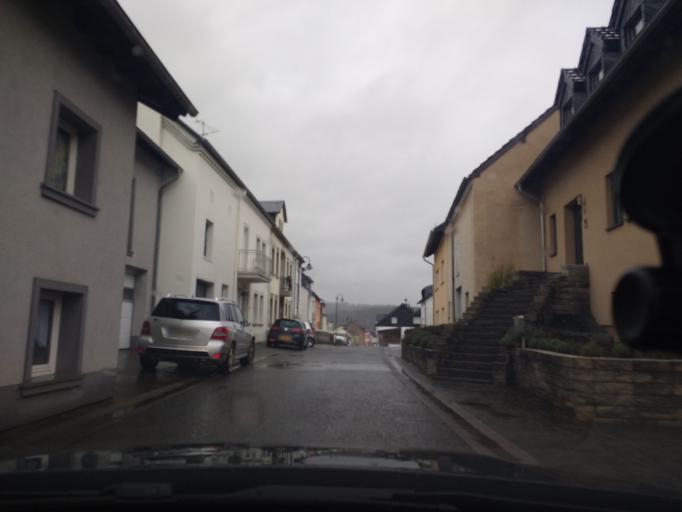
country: DE
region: Rheinland-Pfalz
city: Nittel
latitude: 49.6530
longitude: 6.4466
